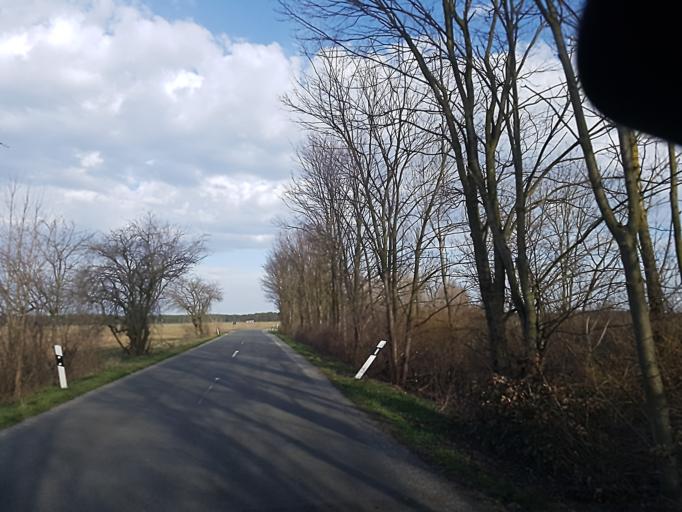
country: DE
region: Brandenburg
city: Falkenberg
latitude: 51.5478
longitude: 13.2988
